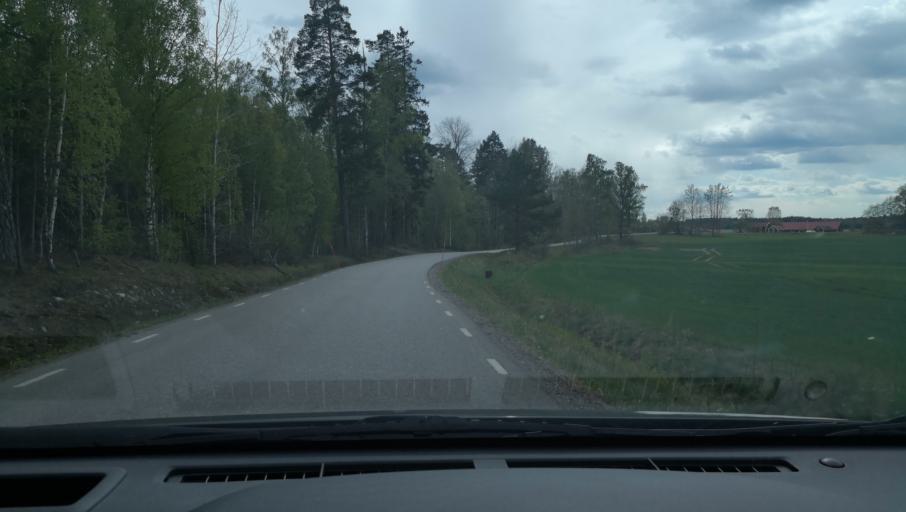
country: SE
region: OErebro
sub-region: Kumla Kommun
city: Kumla
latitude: 59.1541
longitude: 15.1762
